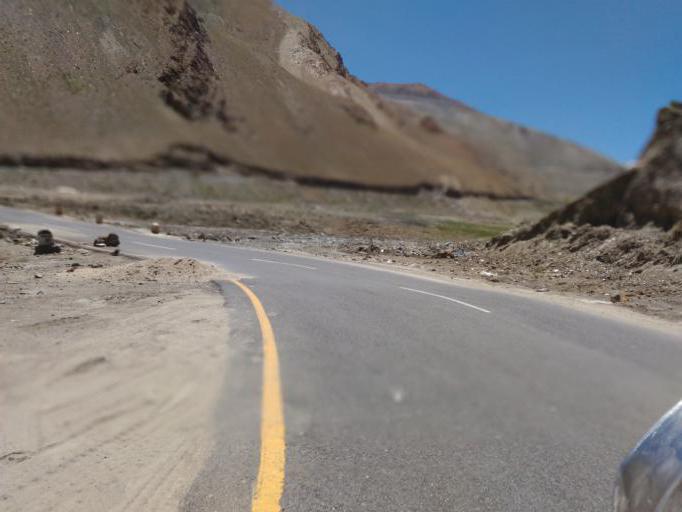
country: IN
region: Kashmir
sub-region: Ladakh
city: Leh
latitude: 33.5820
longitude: 77.7480
